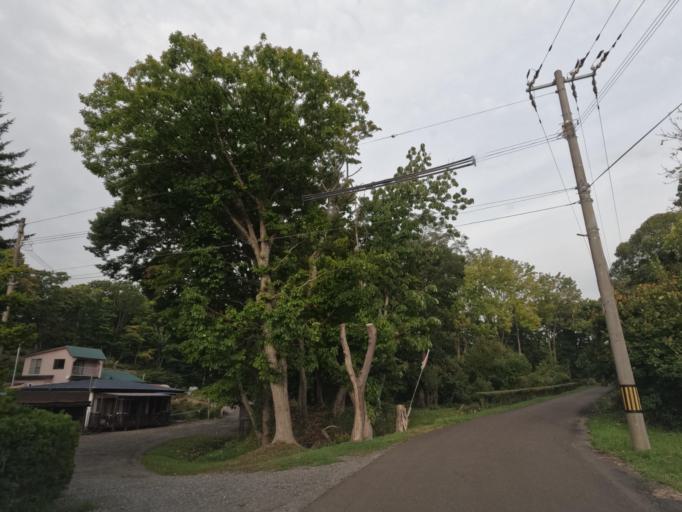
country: JP
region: Hokkaido
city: Date
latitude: 42.4128
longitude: 140.9168
